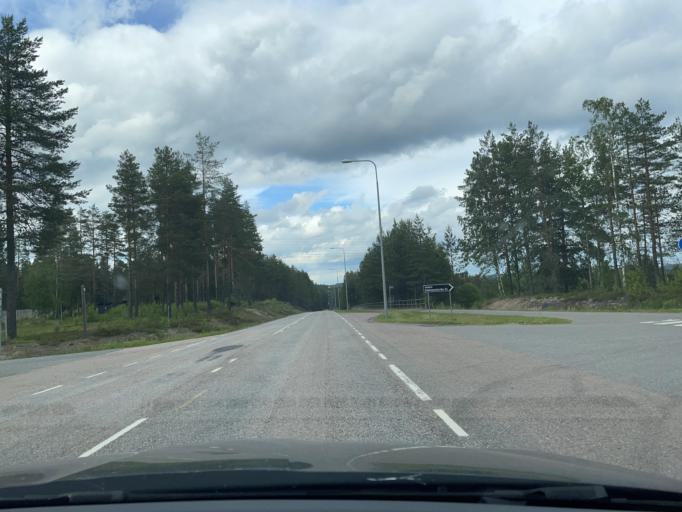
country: FI
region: Central Finland
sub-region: Jaemsae
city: Jaemsaenkoski
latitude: 61.9141
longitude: 25.1451
